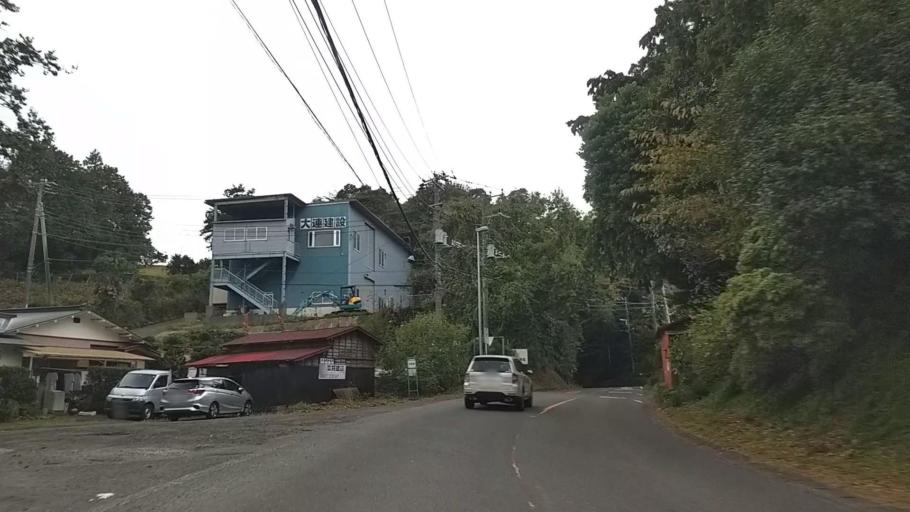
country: JP
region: Kanagawa
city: Yugawara
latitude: 35.1738
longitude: 139.1361
